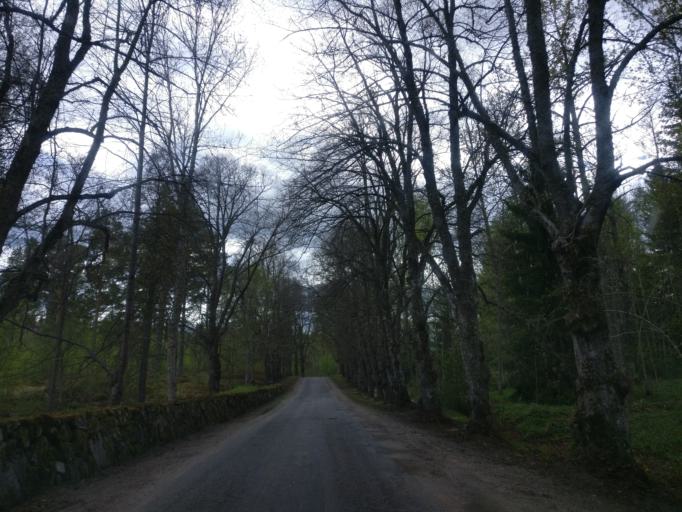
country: SE
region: Gaevleborg
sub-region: Soderhamns Kommun
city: Marielund
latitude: 61.4585
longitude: 17.1167
